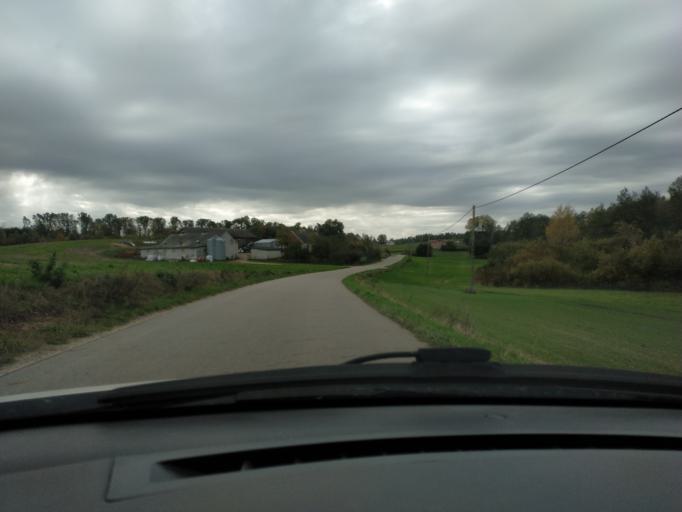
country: PL
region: Warmian-Masurian Voivodeship
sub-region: Powiat nowomiejski
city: Biskupiec
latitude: 53.4587
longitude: 19.3176
